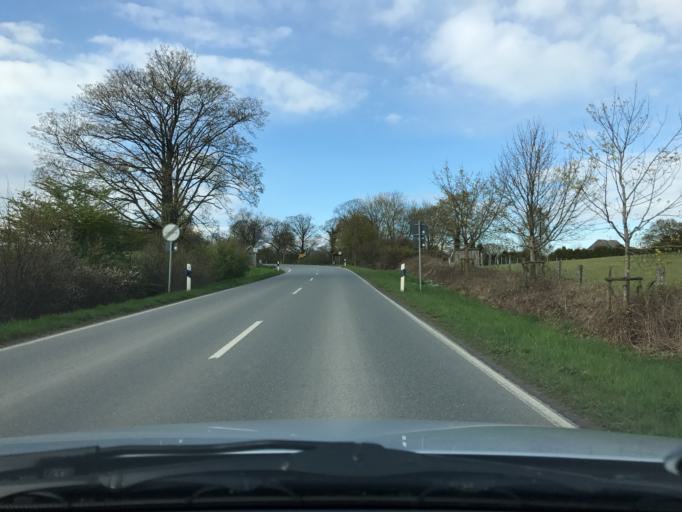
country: DE
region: Schleswig-Holstein
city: Schonwalde am Bungsberg
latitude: 54.1962
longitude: 10.7553
